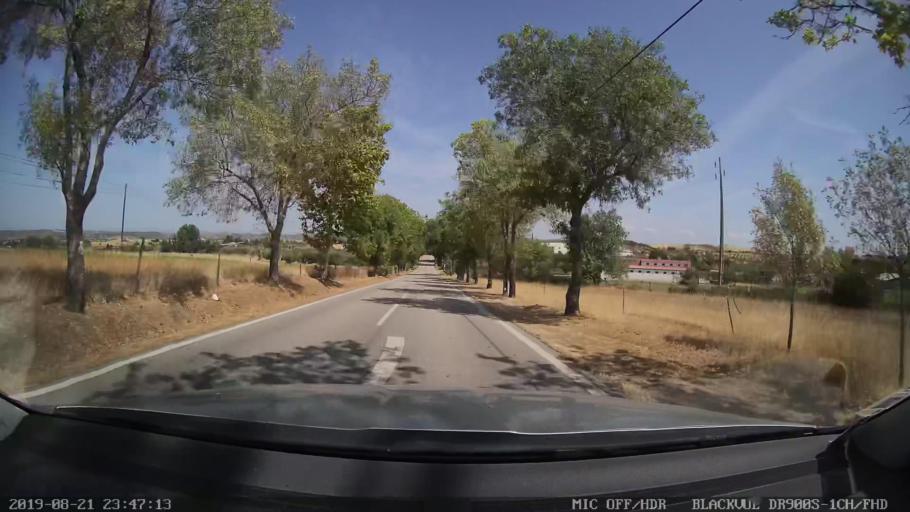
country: PT
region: Castelo Branco
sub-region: Idanha-A-Nova
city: Idanha-a-Nova
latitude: 39.8488
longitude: -7.2571
